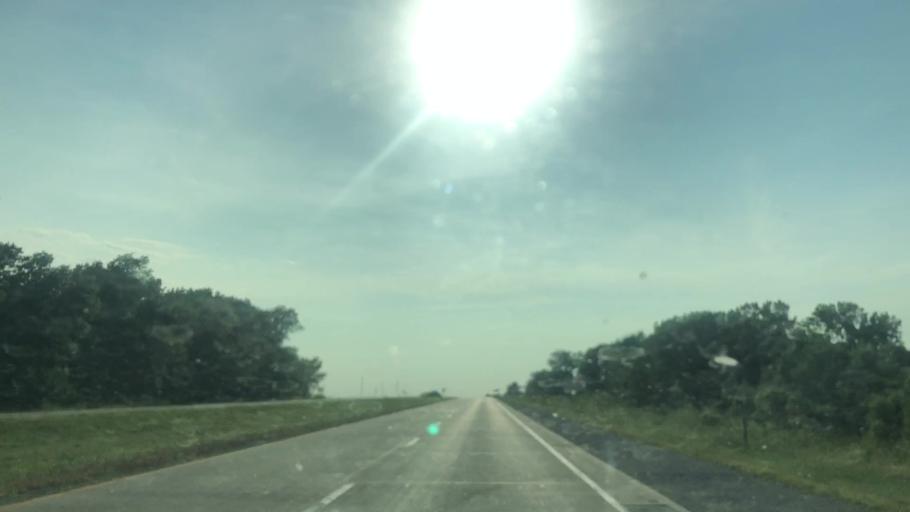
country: US
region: Iowa
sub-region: Story County
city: Nevada
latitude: 42.0078
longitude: -93.3874
